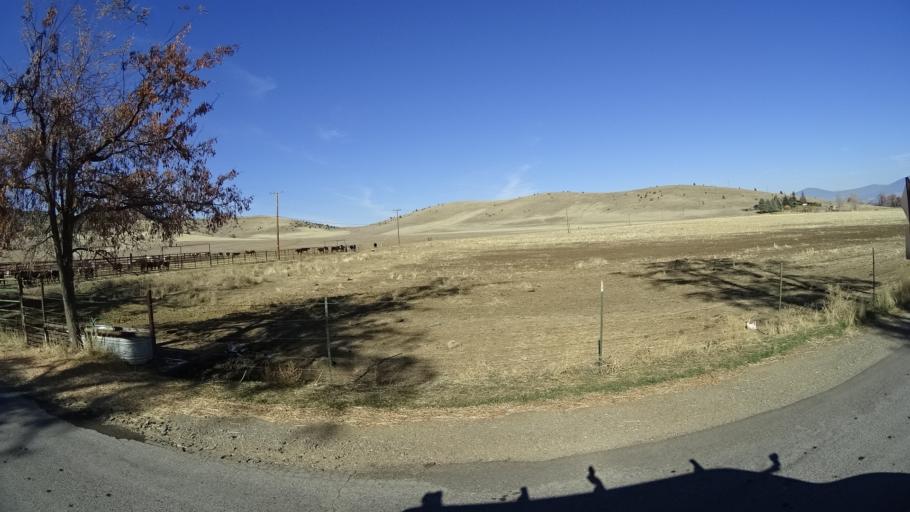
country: US
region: California
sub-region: Siskiyou County
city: Montague
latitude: 41.5971
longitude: -122.5379
